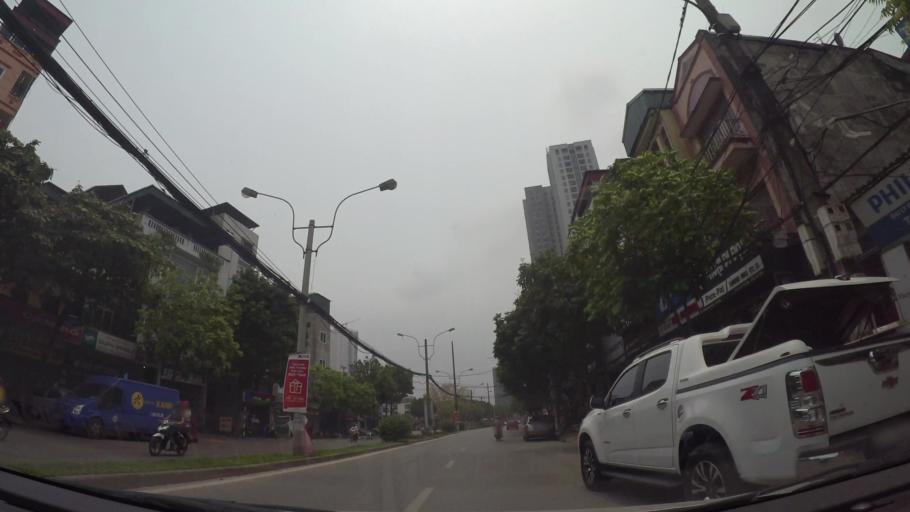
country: VN
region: Ha Noi
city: Ha Dong
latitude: 20.9781
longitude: 105.7746
